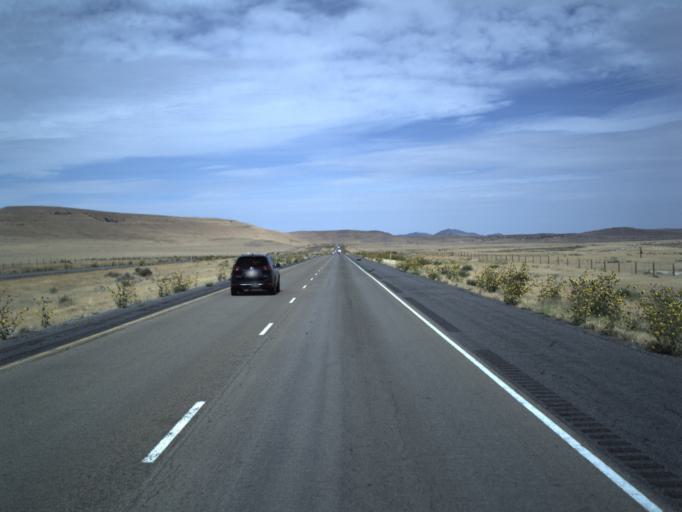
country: US
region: Utah
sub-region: Tooele County
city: Grantsville
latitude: 40.7990
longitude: -112.8472
